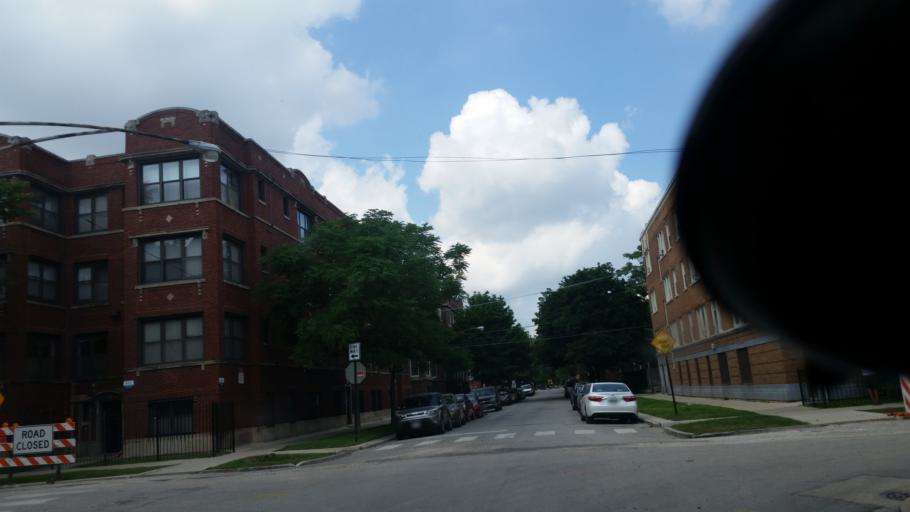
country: US
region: Illinois
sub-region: Cook County
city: Chicago
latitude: 41.7680
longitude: -87.5737
